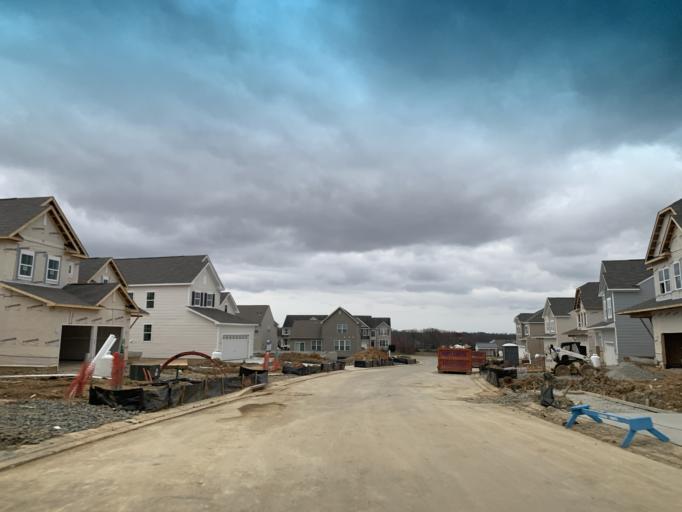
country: US
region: Maryland
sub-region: Harford County
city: Perryman
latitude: 39.4982
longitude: -76.2076
